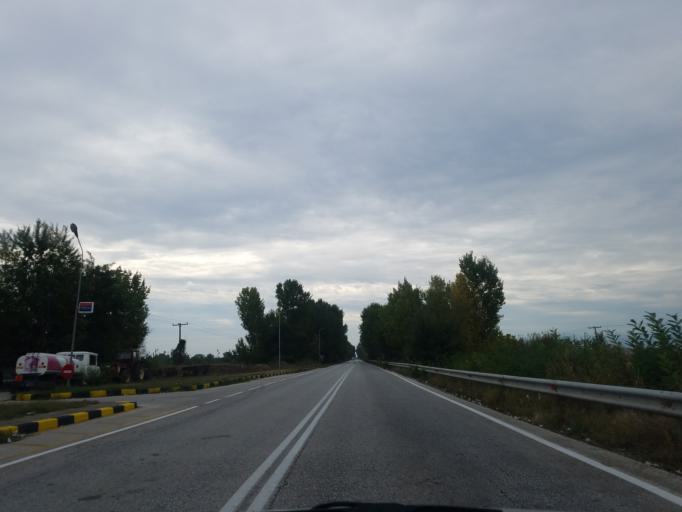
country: GR
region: Thessaly
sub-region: Nomos Kardhitsas
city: Agnantero
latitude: 39.4669
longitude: 21.8513
